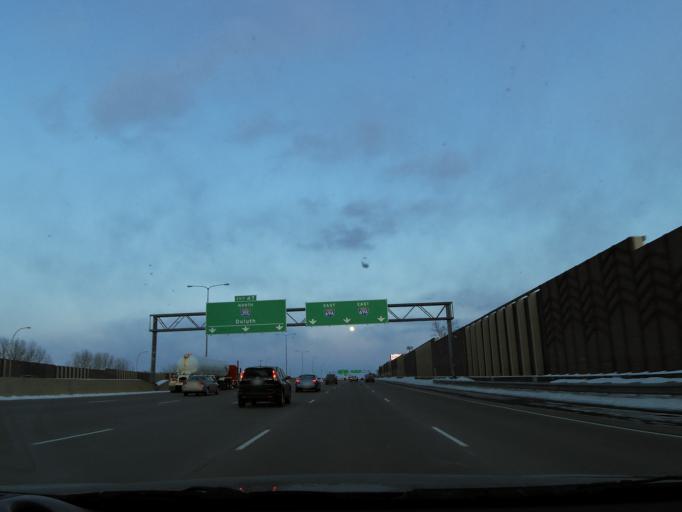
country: US
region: Minnesota
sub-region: Ramsey County
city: Little Canada
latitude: 45.0365
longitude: -93.0730
